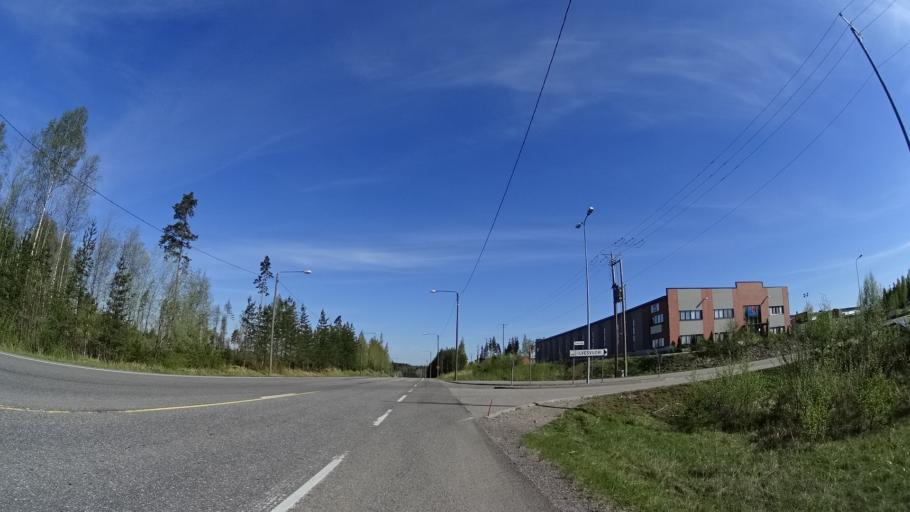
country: FI
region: Uusimaa
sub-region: Helsinki
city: Nurmijaervi
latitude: 60.4520
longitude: 24.8335
